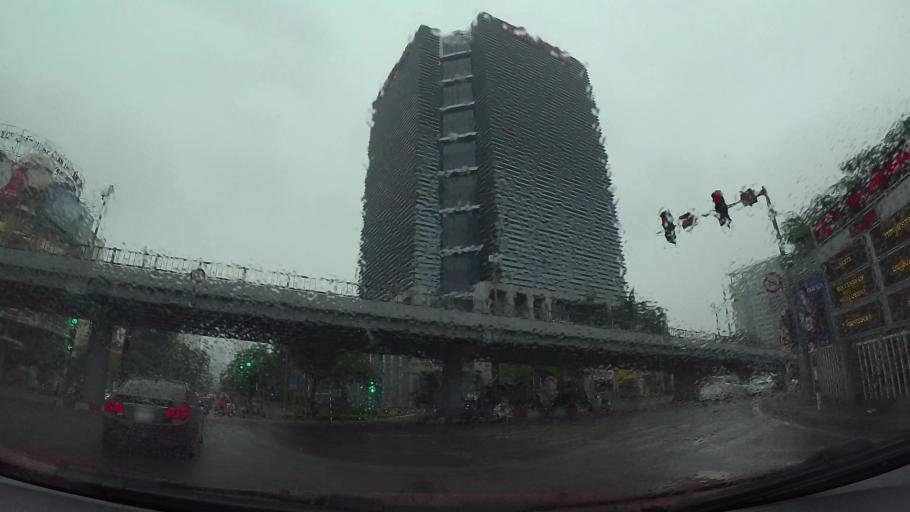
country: VN
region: Ha Noi
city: Dong Da
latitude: 21.0165
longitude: 105.8151
